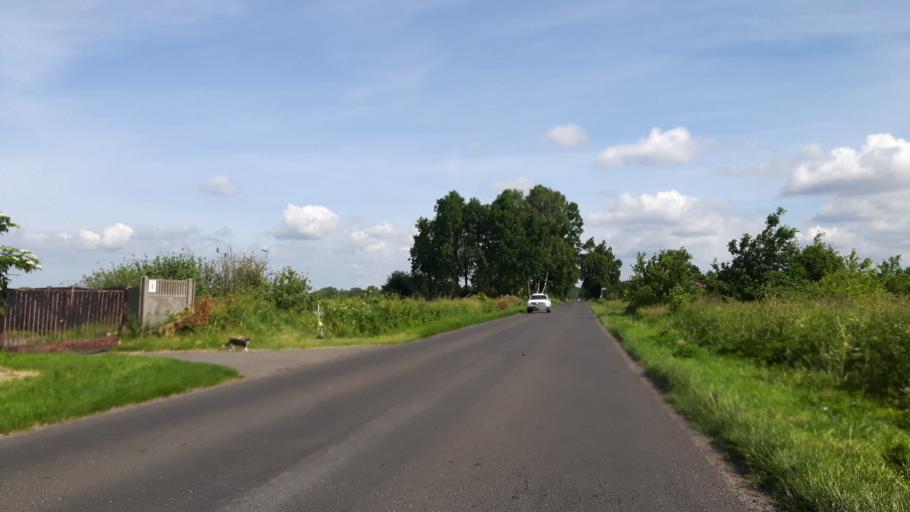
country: PL
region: West Pomeranian Voivodeship
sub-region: Powiat goleniowski
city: Goleniow
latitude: 53.4704
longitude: 14.7735
